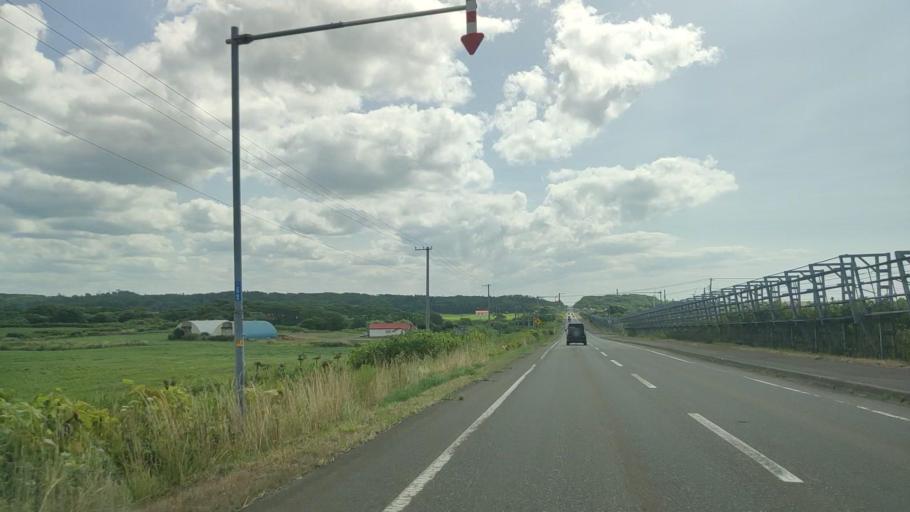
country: JP
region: Hokkaido
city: Makubetsu
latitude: 44.7766
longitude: 141.7916
